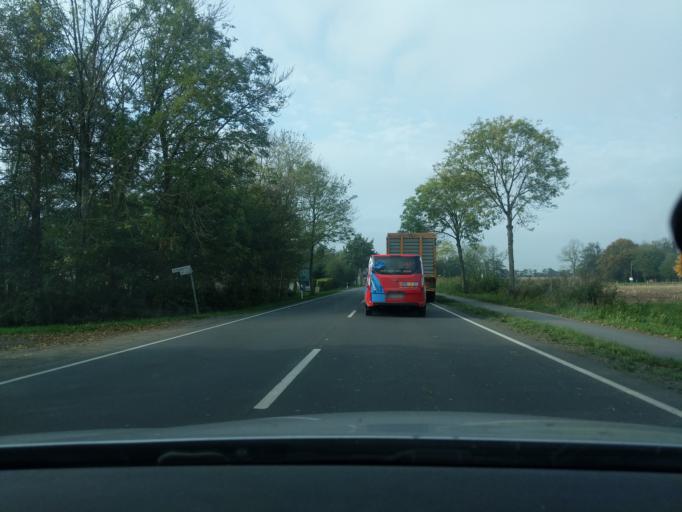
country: DE
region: Lower Saxony
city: Belum
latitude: 53.8184
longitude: 8.9823
